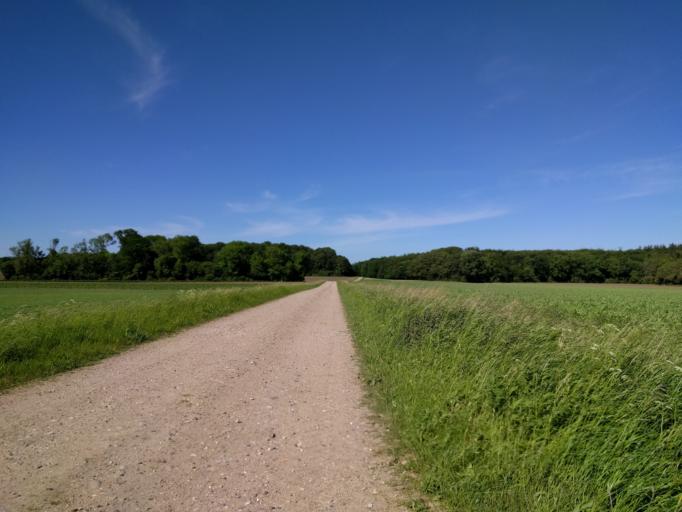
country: DK
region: South Denmark
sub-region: Kerteminde Kommune
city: Kerteminde
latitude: 55.4318
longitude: 10.6663
